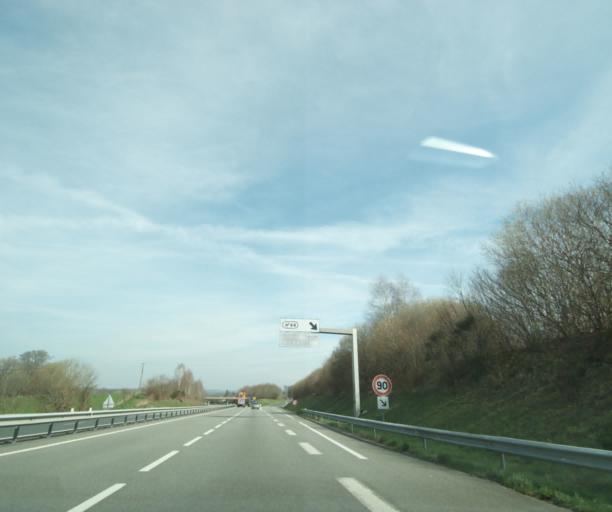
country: FR
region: Limousin
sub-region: Departement de la Correze
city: Uzerche
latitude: 45.4782
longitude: 1.5262
